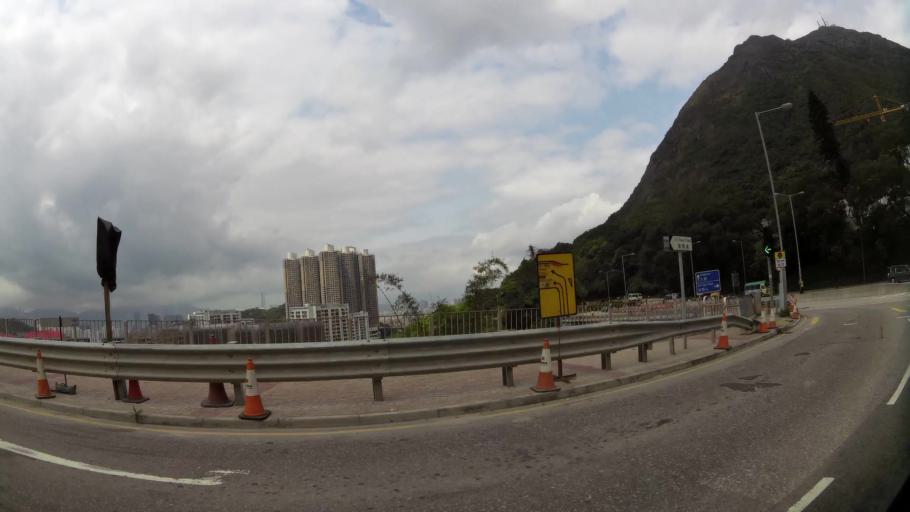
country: HK
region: Wong Tai Sin
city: Wong Tai Sin
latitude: 22.3340
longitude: 114.2283
